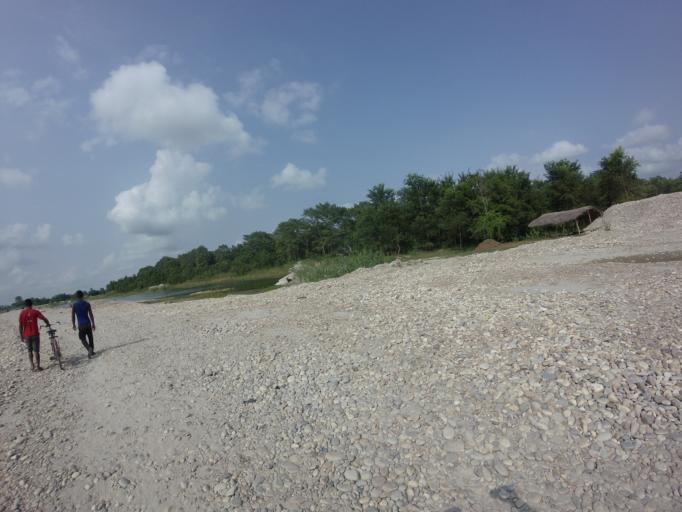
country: NP
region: Far Western
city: Tikapur
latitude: 28.4468
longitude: 81.0752
